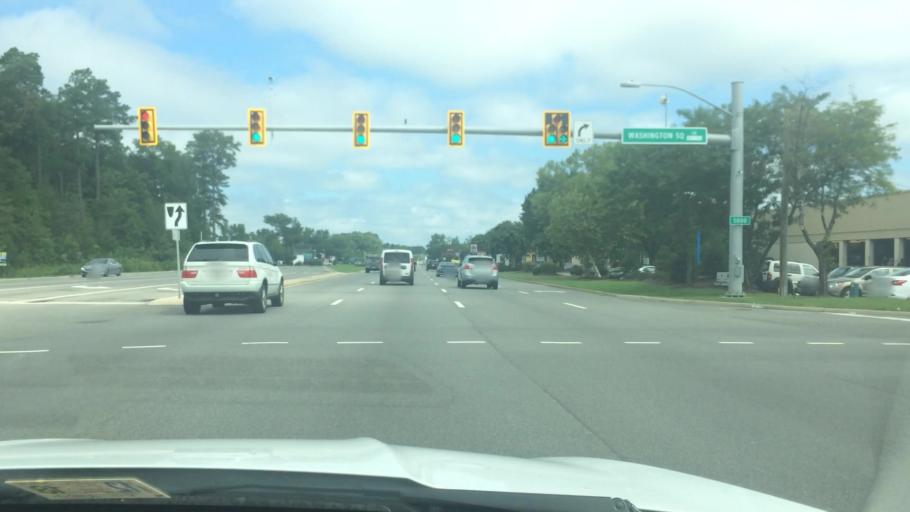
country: US
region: Virginia
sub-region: York County
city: Yorktown
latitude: 37.1556
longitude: -76.4618
